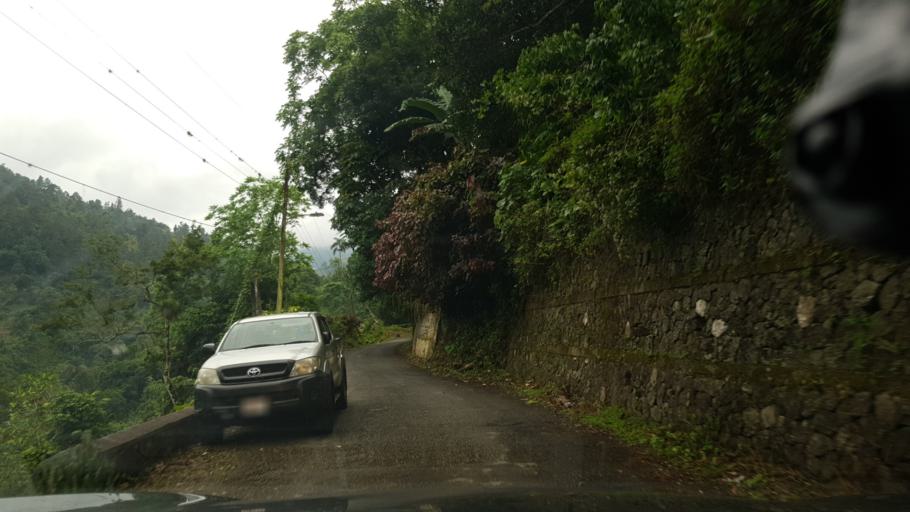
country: JM
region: Saint Andrew
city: Stony Hill
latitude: 18.1257
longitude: -76.7159
